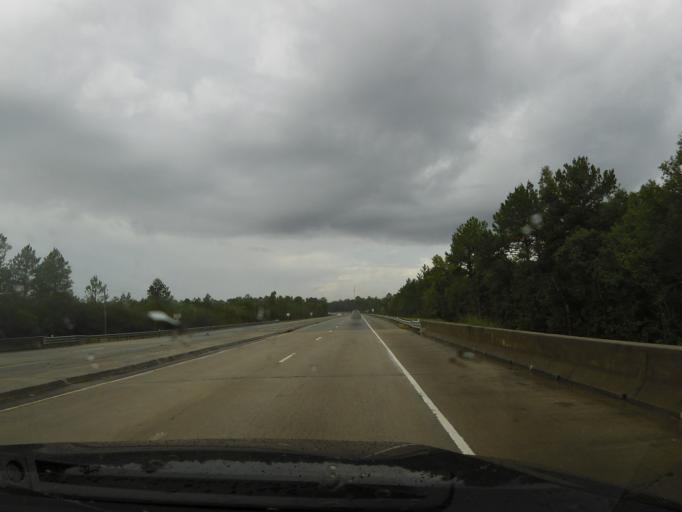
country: US
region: Georgia
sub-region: Wayne County
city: Jesup
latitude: 31.5696
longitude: -81.8414
